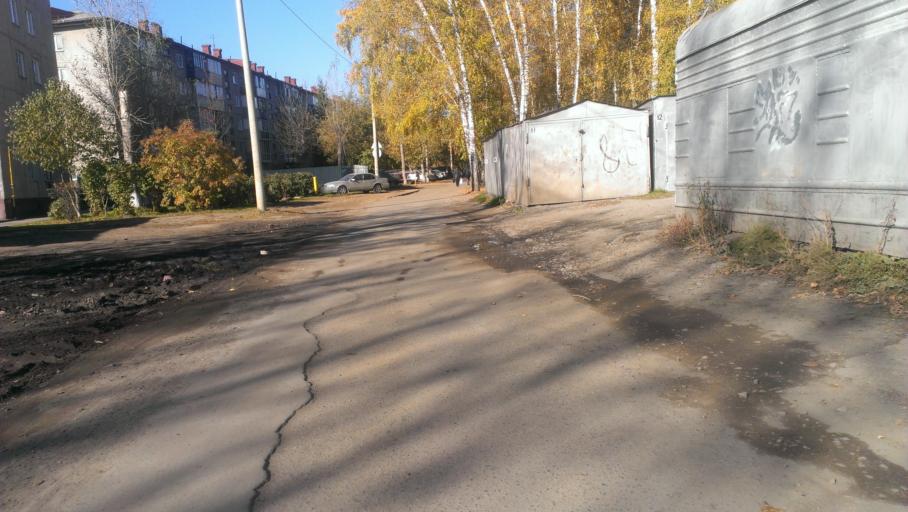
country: RU
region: Altai Krai
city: Novosilikatnyy
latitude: 53.3634
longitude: 83.6831
